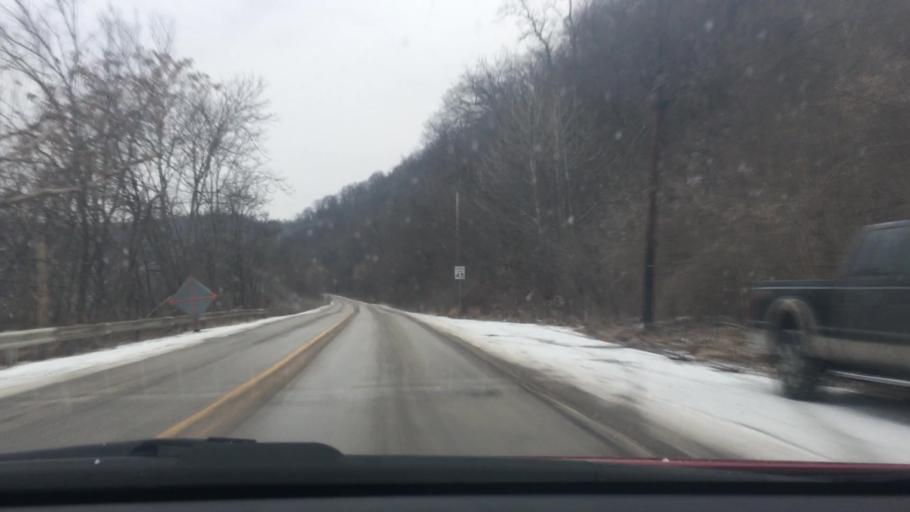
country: US
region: Pennsylvania
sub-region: Washington County
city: New Eagle
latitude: 40.2404
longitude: -79.9631
